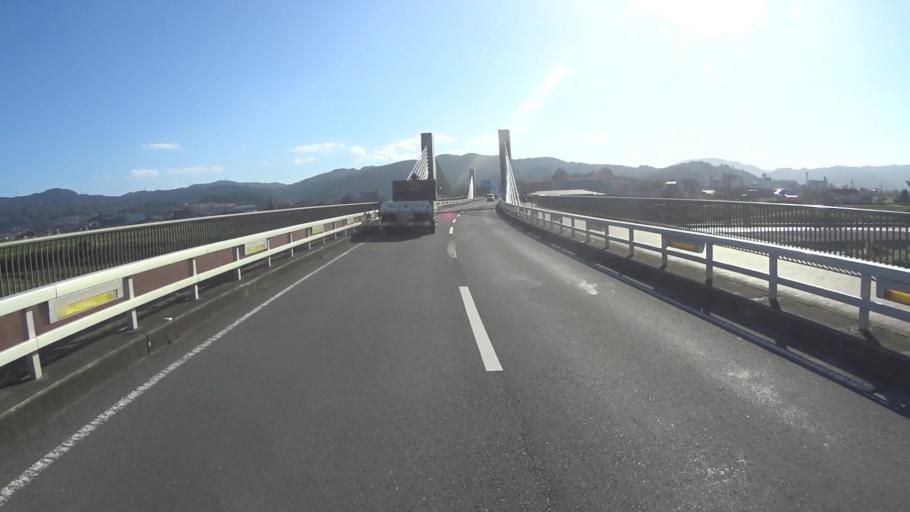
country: JP
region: Kyoto
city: Kameoka
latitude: 35.0189
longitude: 135.5889
